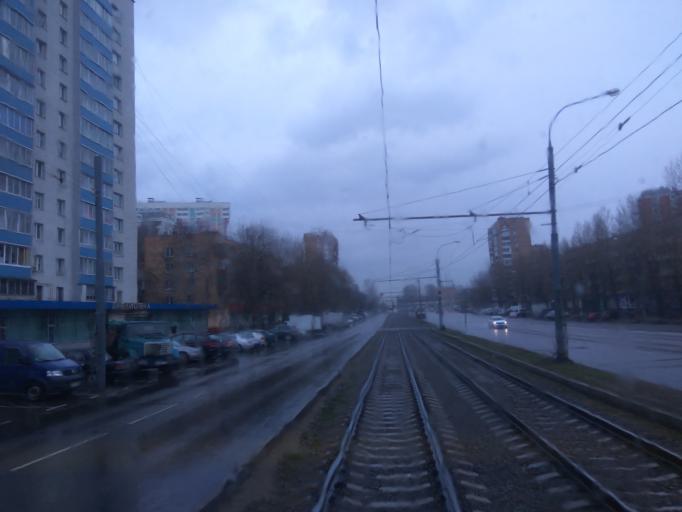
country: RU
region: Moscow
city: Kozeyevo
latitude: 55.8751
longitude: 37.6368
